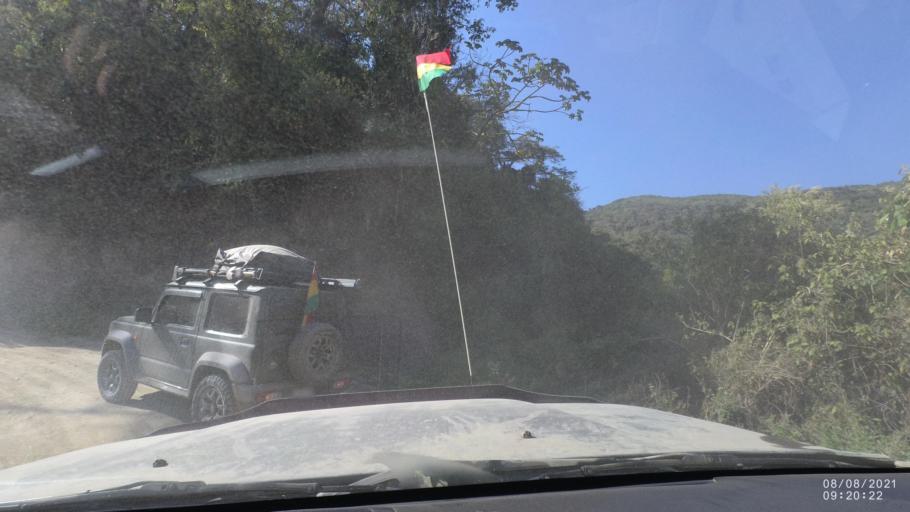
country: BO
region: La Paz
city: Quime
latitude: -16.5730
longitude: -66.7180
